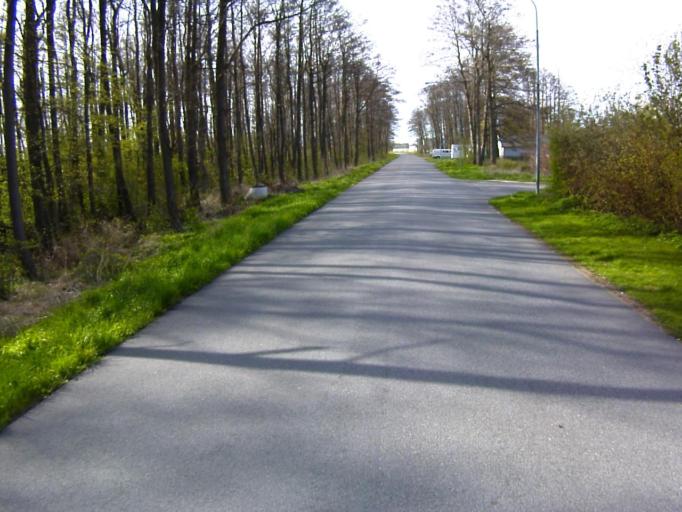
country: SE
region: Skane
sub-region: Kristianstads Kommun
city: Kristianstad
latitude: 56.0108
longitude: 14.1562
